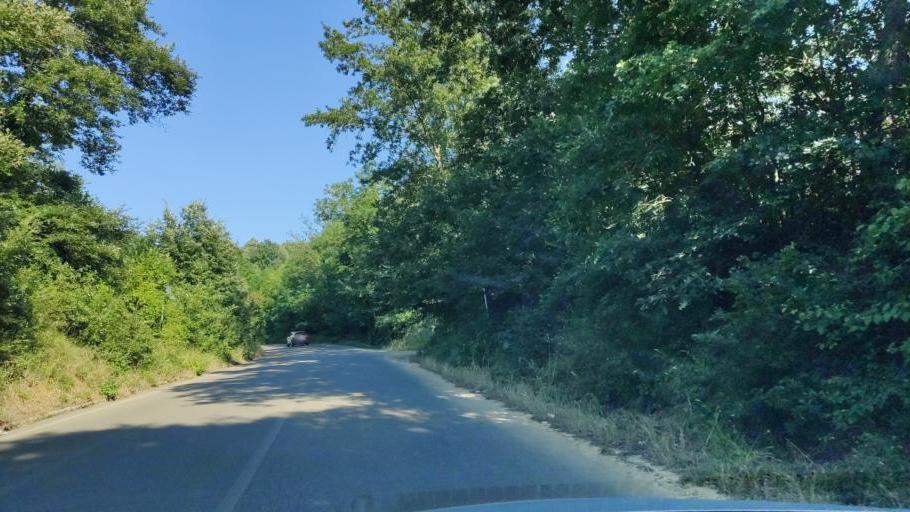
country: IT
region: Umbria
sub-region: Provincia di Terni
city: Penna in Teverina
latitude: 42.4787
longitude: 12.3687
